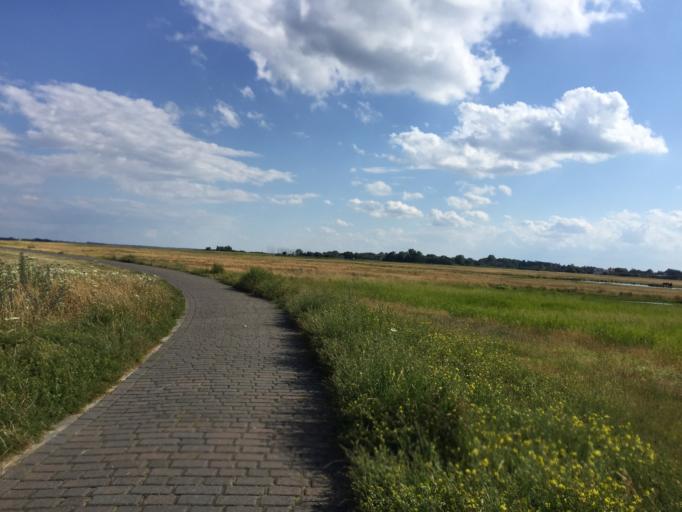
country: DE
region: Mecklenburg-Vorpommern
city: Hiddensee
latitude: 54.5823
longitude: 13.1087
